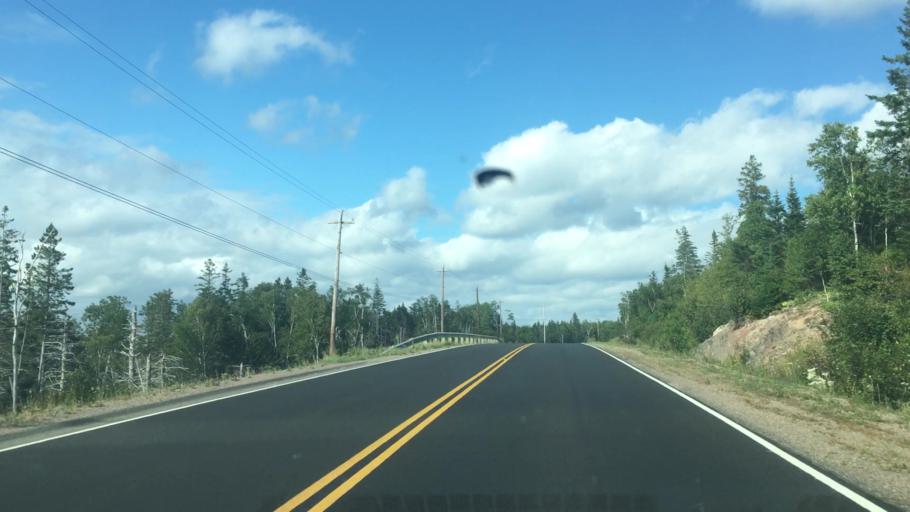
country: CA
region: Nova Scotia
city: Princeville
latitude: 45.8091
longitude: -60.7079
